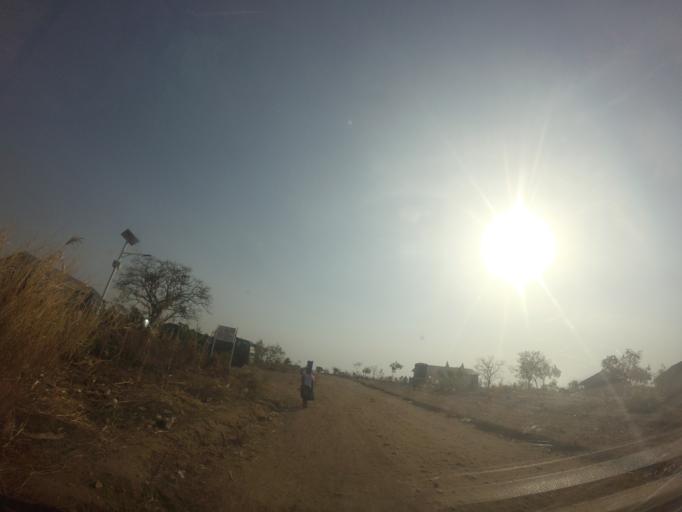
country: UG
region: Northern Region
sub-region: Maracha District
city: Maracha
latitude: 3.1203
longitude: 31.1582
